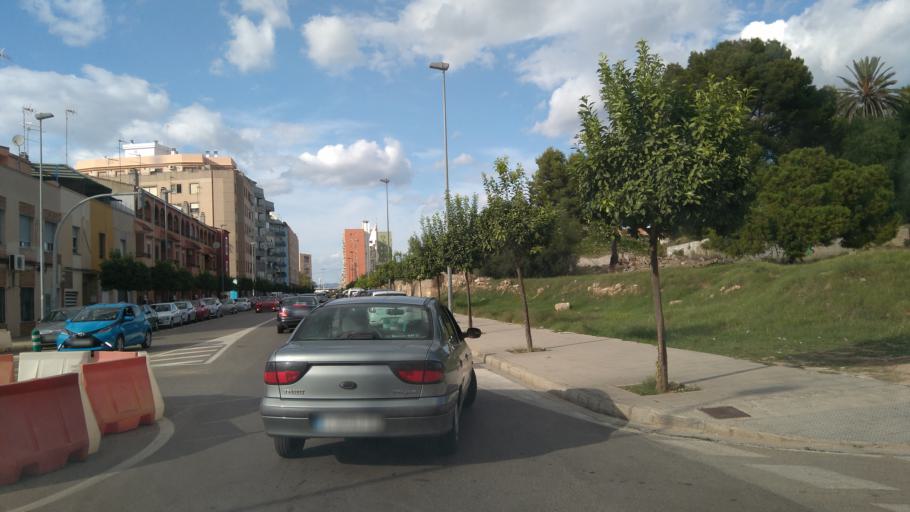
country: ES
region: Valencia
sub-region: Provincia de Valencia
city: Alzira
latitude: 39.1542
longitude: -0.4265
